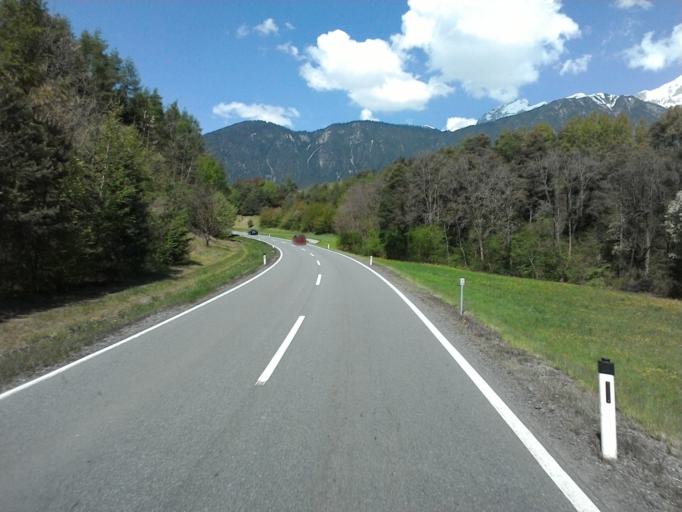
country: AT
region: Tyrol
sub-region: Politischer Bezirk Imst
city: Mieming
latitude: 47.2969
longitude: 10.9686
